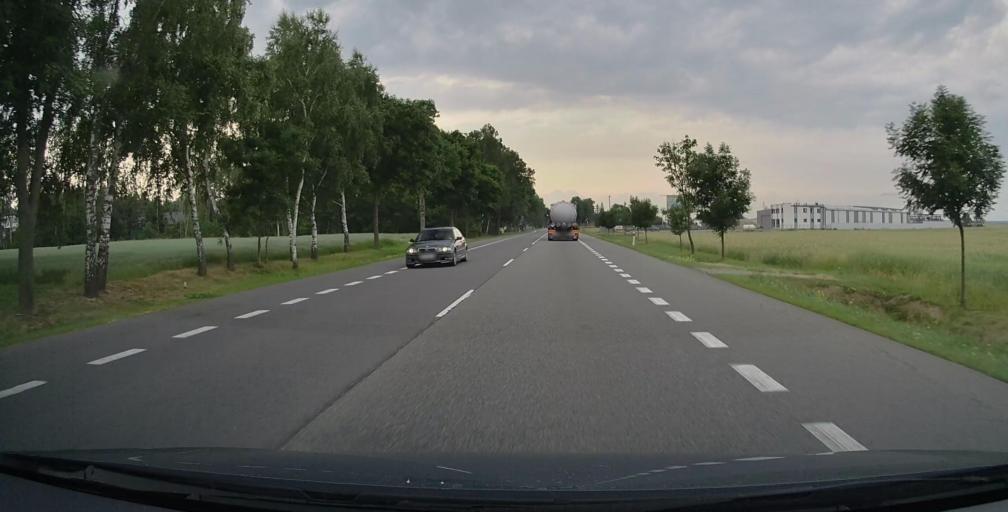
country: PL
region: Masovian Voivodeship
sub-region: Powiat siedlecki
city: Zbuczyn
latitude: 52.0948
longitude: 22.4187
